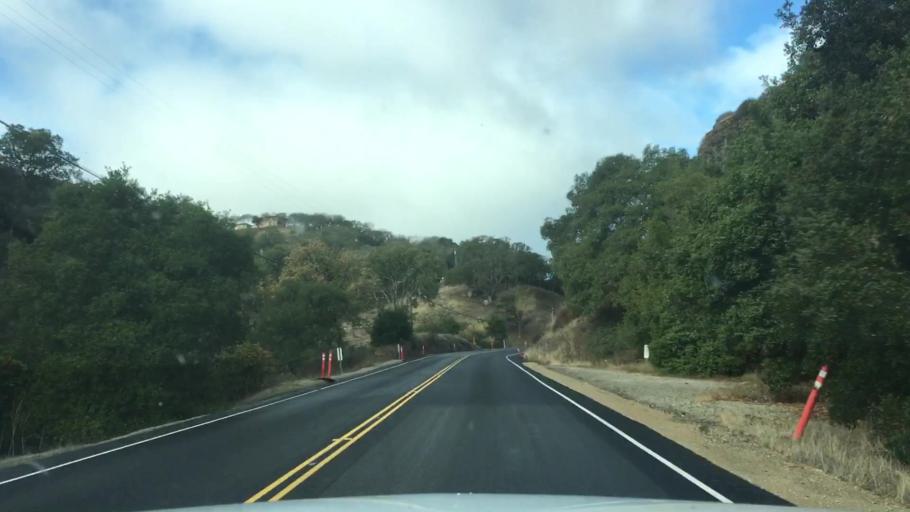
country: US
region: California
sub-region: San Luis Obispo County
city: Atascadero
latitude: 35.4515
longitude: -120.7067
